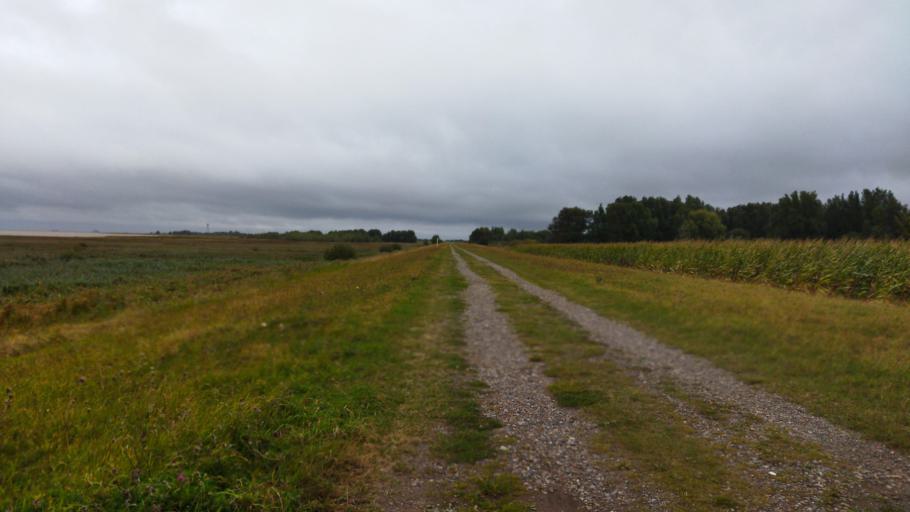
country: NL
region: Groningen
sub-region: Gemeente Delfzijl
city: Delfzijl
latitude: 53.3708
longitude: 7.0086
